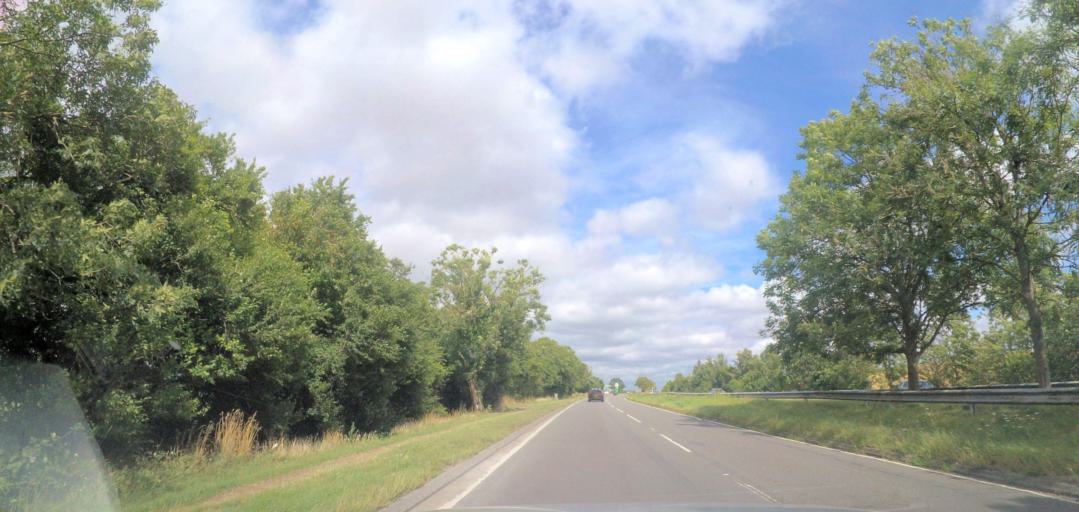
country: GB
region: England
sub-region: Cambridgeshire
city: Bassingbourn
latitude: 52.0277
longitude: -0.1092
